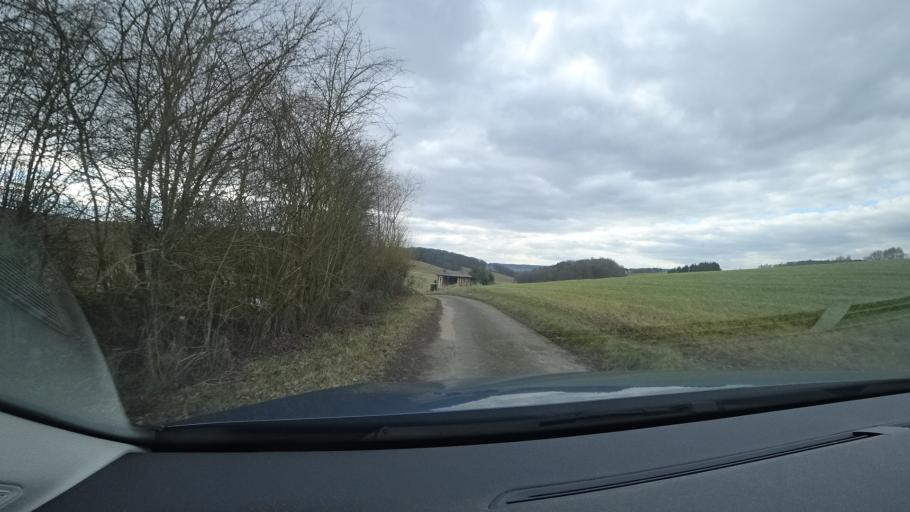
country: DE
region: Rheinland-Pfalz
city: Hunzel
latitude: 50.2470
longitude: 7.8325
